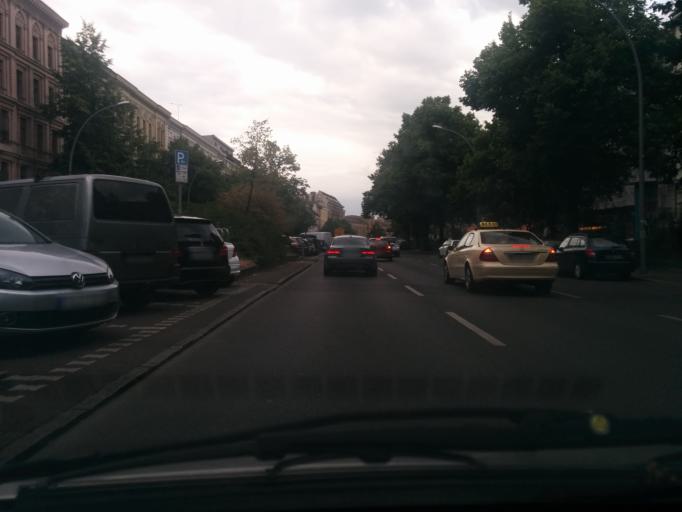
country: DE
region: Berlin
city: Bezirk Kreuzberg
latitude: 52.4910
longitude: 13.3868
